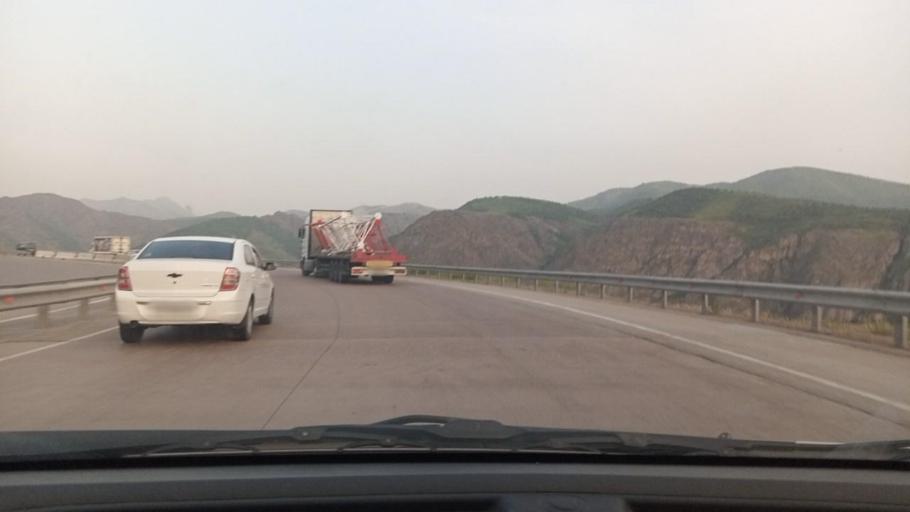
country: UZ
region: Toshkent
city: Angren
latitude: 41.0735
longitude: 70.2551
